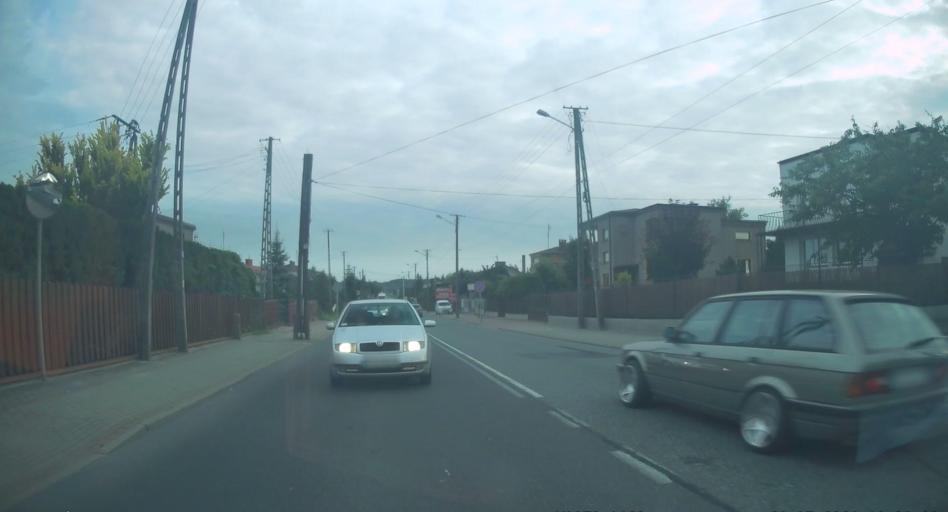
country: PL
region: Lodz Voivodeship
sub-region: Powiat radomszczanski
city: Kamiensk
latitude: 51.2004
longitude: 19.4998
